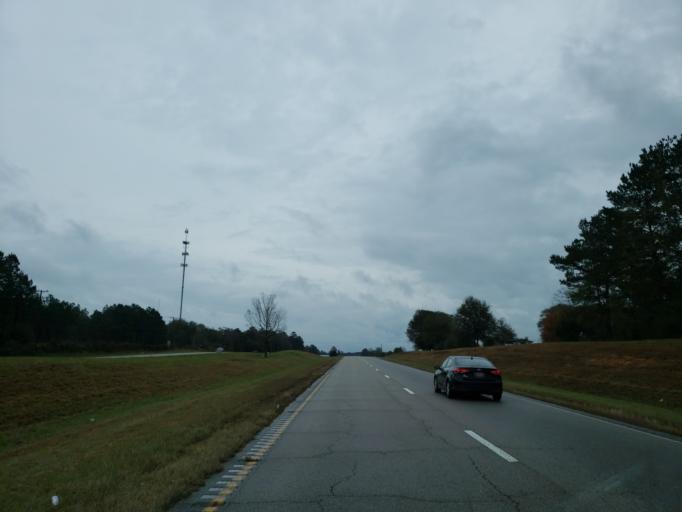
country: US
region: Mississippi
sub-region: Jones County
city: Sharon
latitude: 31.7046
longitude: -88.9244
